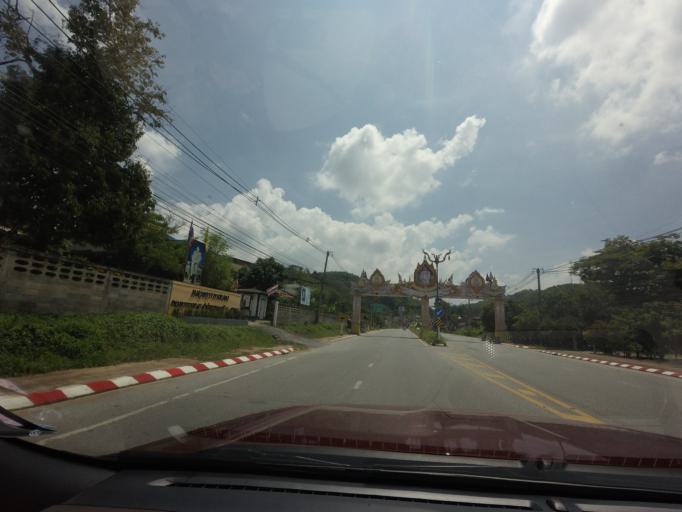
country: TH
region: Yala
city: Betong
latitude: 5.7860
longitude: 101.0725
